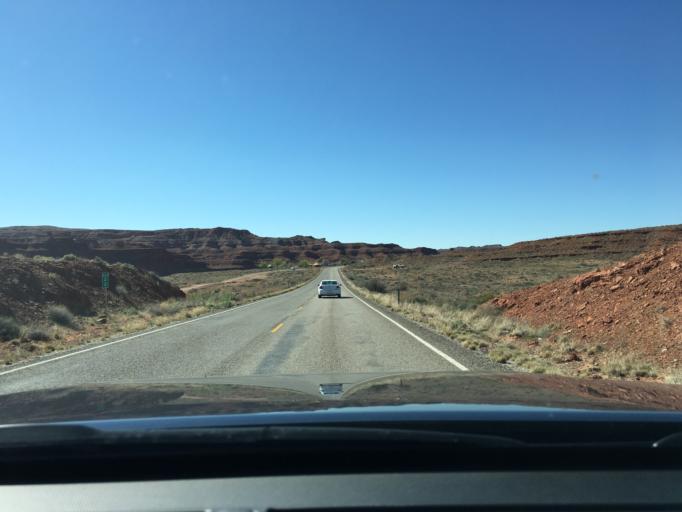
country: US
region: Arizona
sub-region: Navajo County
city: Kayenta
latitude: 37.1558
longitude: -109.8572
